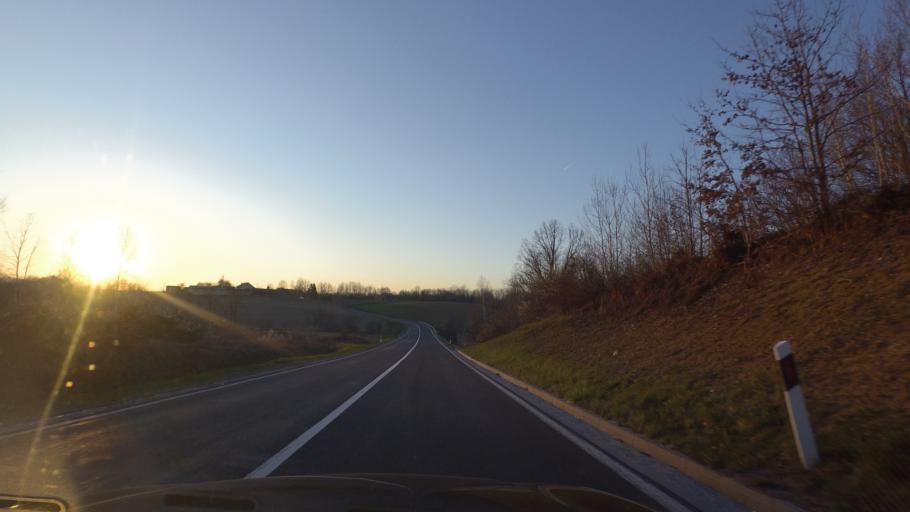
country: HR
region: Sisacko-Moslavacka
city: Gvozd
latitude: 45.3274
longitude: 15.9378
